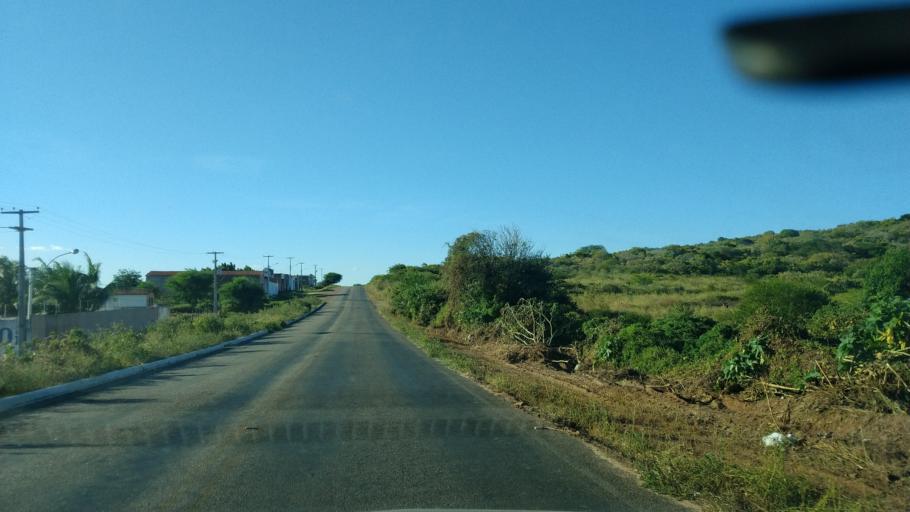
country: BR
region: Rio Grande do Norte
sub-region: Sao Jose Do Campestre
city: Sao Jose do Campestre
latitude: -6.3096
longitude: -35.7157
